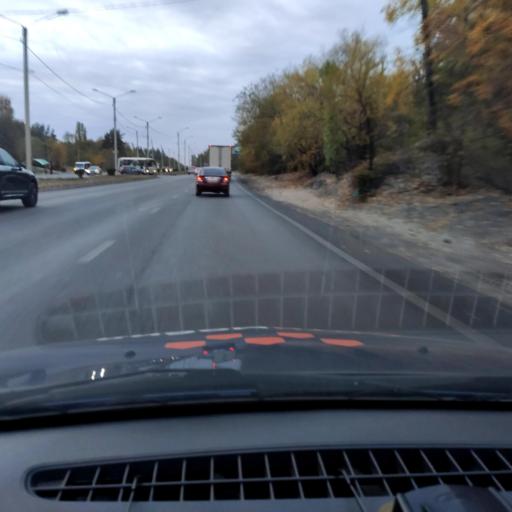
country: RU
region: Voronezj
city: Pridonskoy
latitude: 51.6726
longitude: 39.1193
